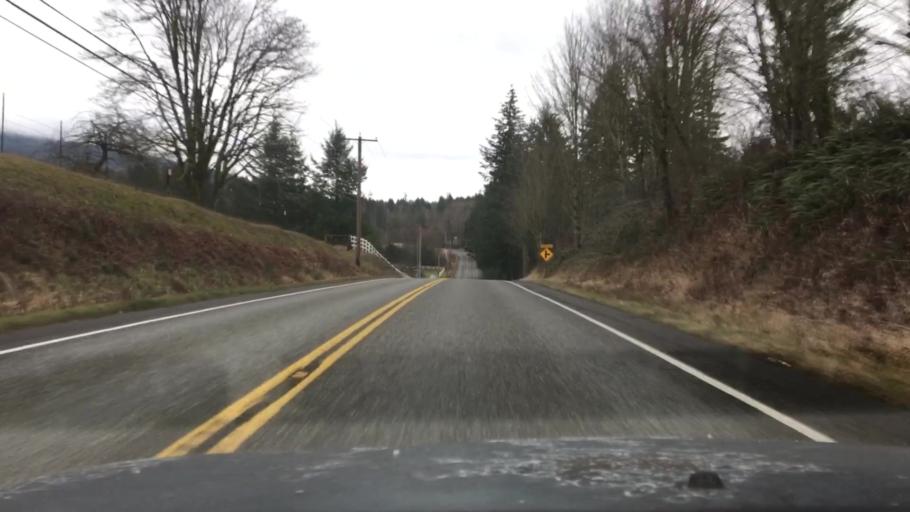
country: US
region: Washington
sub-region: Whatcom County
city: Sudden Valley
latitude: 48.6512
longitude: -122.3243
